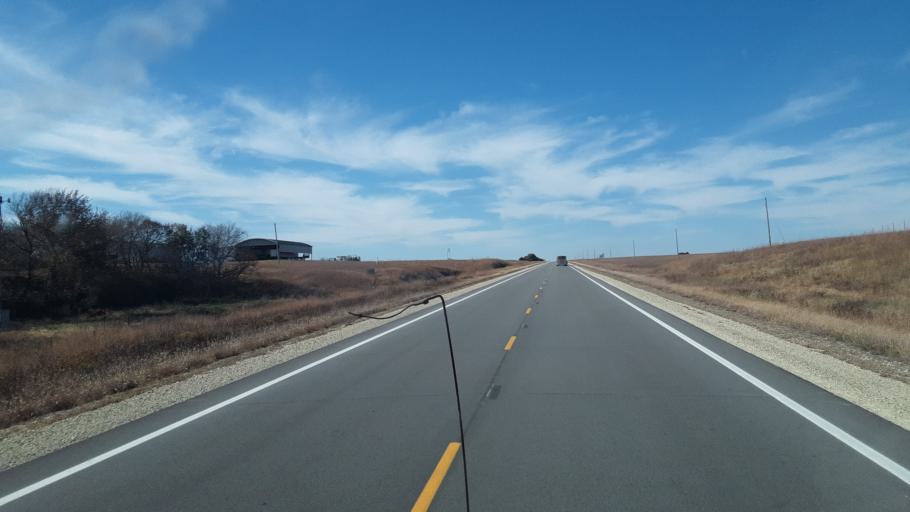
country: US
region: Kansas
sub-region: Marion County
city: Marion
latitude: 38.3628
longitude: -96.7870
